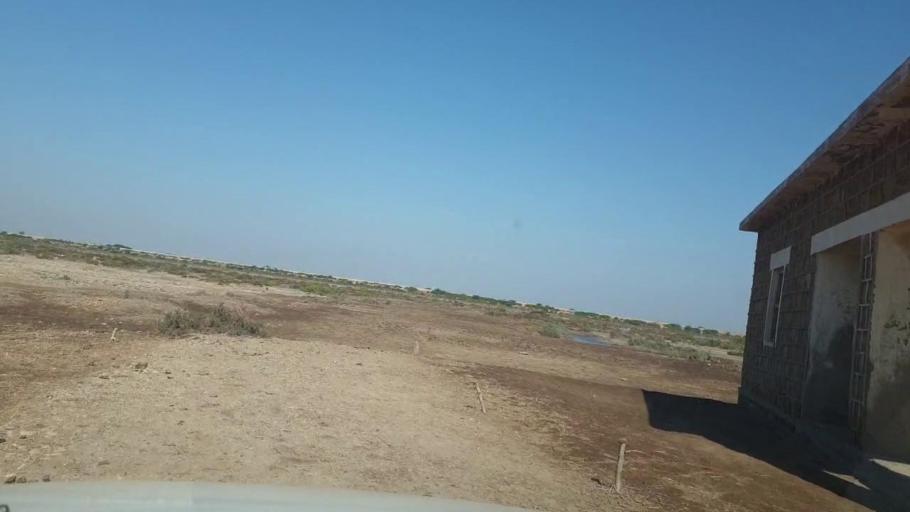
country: PK
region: Sindh
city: Chuhar Jamali
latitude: 24.4374
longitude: 67.8406
